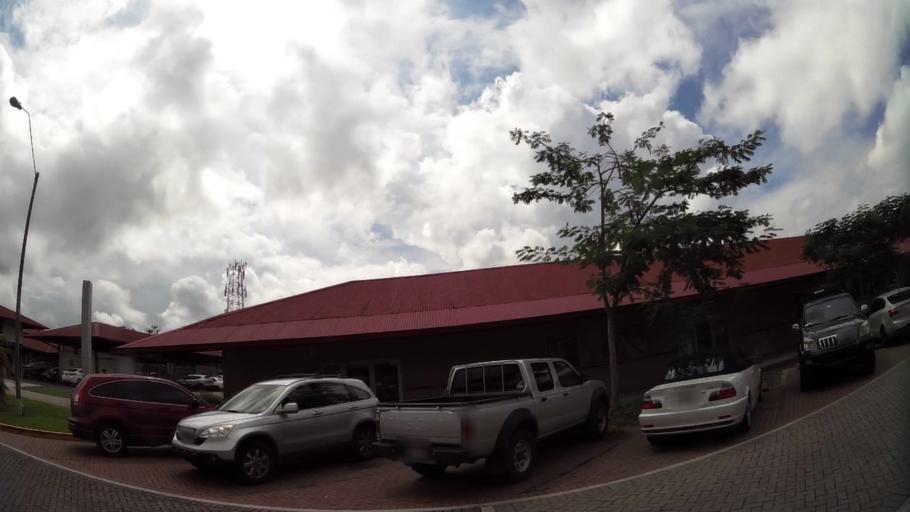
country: PA
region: Panama
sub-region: Distrito de Panama
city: Ancon
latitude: 9.0024
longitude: -79.5830
